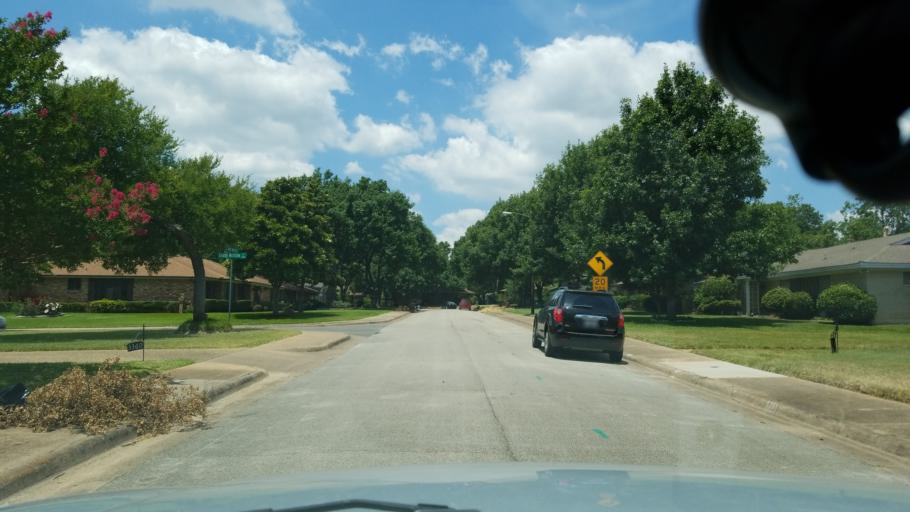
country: US
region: Texas
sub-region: Dallas County
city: Cockrell Hill
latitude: 32.6935
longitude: -96.8763
